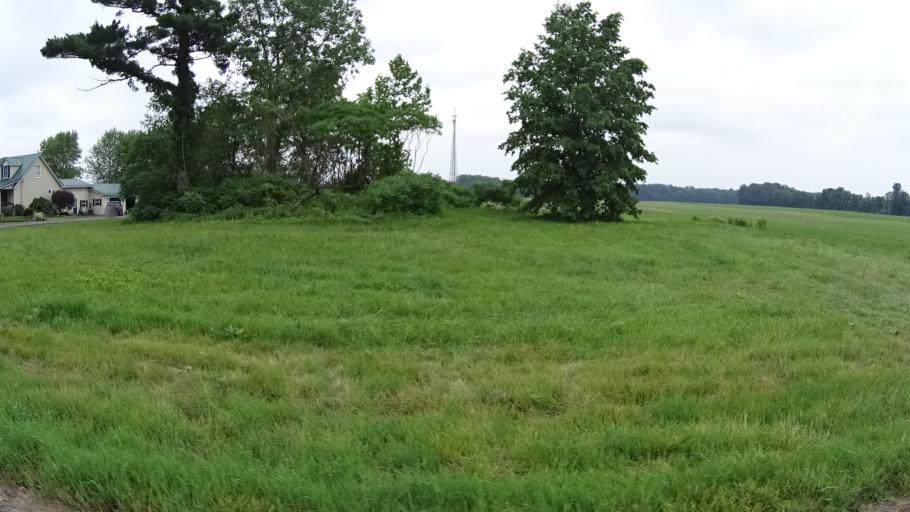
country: US
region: Ohio
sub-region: Erie County
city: Milan
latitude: 41.2991
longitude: -82.5664
